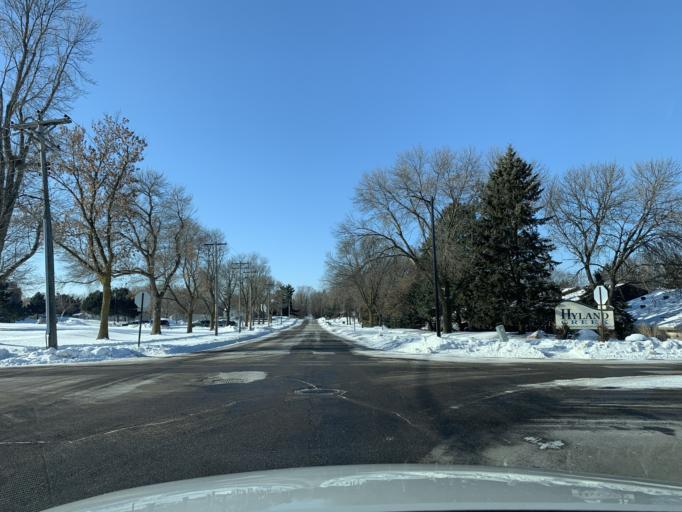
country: US
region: Minnesota
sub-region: Hennepin County
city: Edina
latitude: 44.8332
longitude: -93.3582
